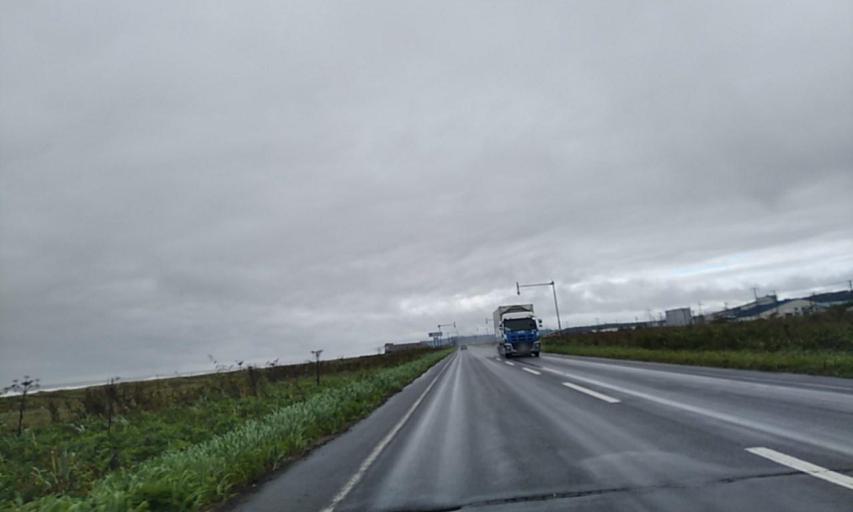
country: JP
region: Hokkaido
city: Kushiro
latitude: 42.9979
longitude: 144.2246
